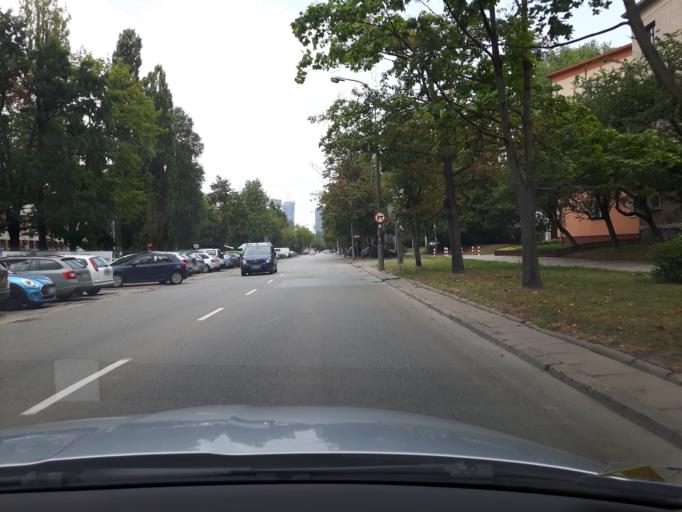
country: PL
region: Masovian Voivodeship
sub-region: Warszawa
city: Ochota
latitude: 52.2164
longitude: 20.9709
